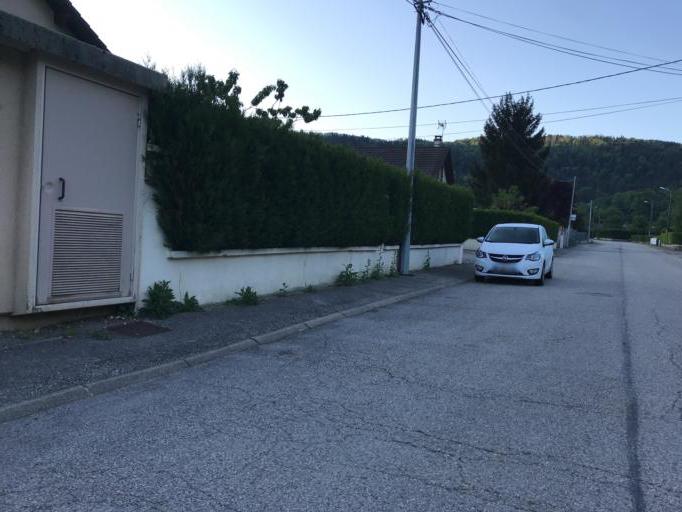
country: FR
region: Rhone-Alpes
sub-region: Departement de l'Ain
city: Oyonnax
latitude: 46.2401
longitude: 5.6673
